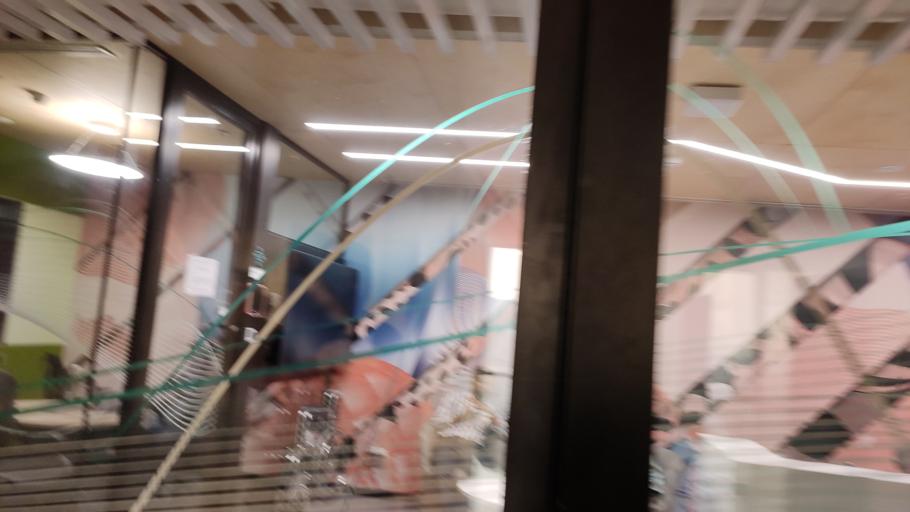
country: IN
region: Maharashtra
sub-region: Mumbai Suburban
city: Powai
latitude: 19.1525
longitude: 72.8547
